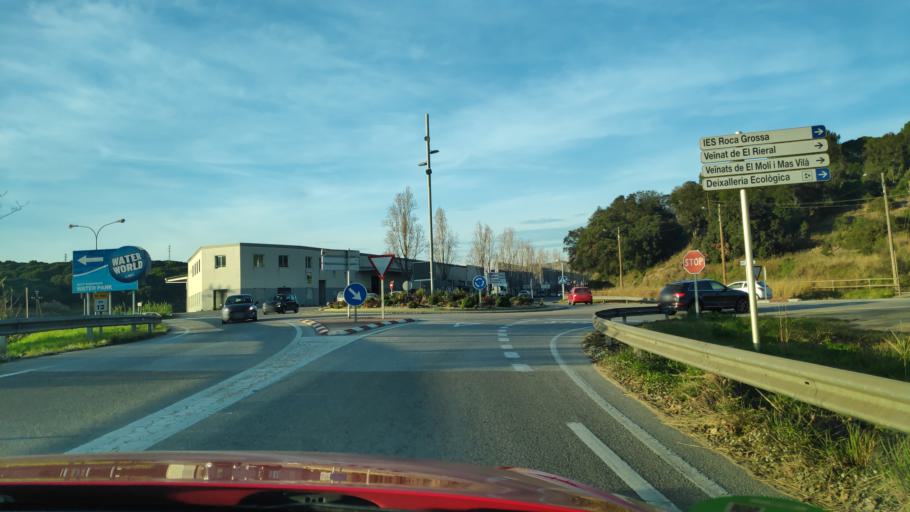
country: ES
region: Catalonia
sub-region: Provincia de Girona
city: Lloret de Mar
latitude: 41.7086
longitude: 2.8327
